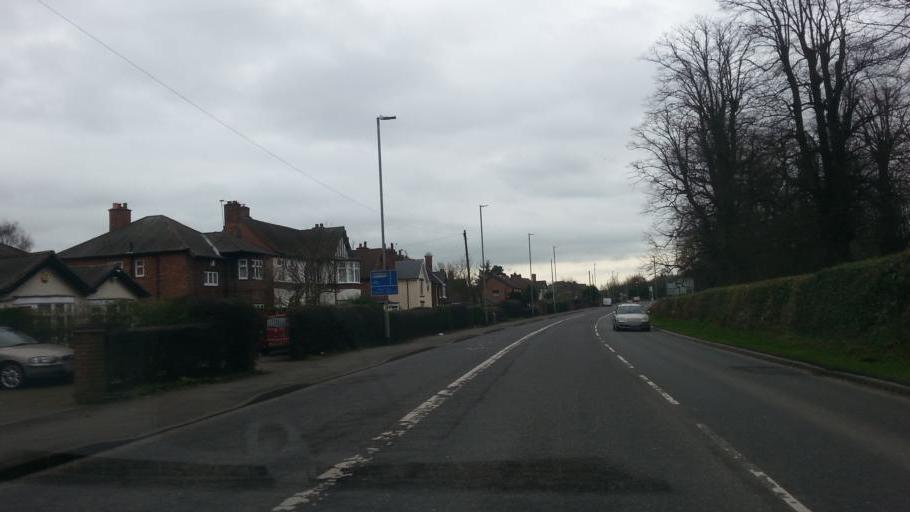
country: GB
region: England
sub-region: Nottinghamshire
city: Kimberley
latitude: 52.9934
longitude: -1.2272
